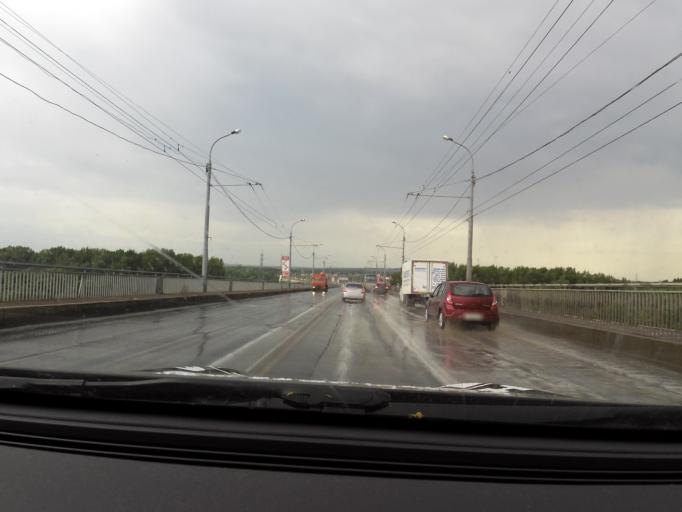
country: RU
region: Bashkortostan
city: Ufa
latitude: 54.7583
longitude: 55.9643
